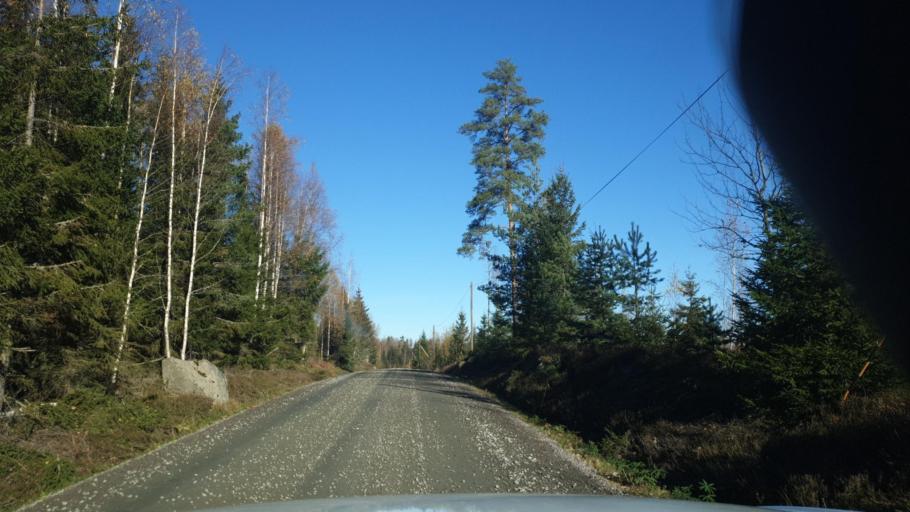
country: SE
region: Vaermland
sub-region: Karlstads Kommun
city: Edsvalla
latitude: 59.5073
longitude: 13.2066
